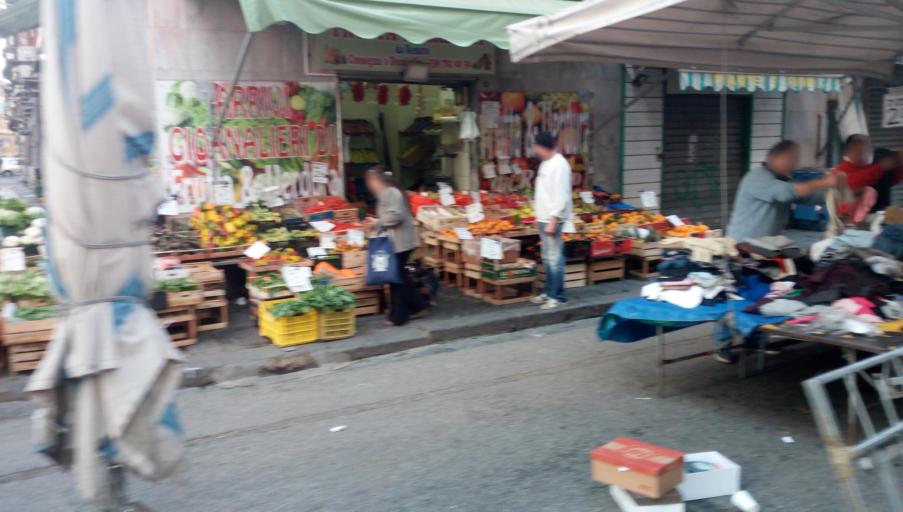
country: IT
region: Campania
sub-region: Provincia di Napoli
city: Napoli
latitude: 40.8556
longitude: 14.2732
